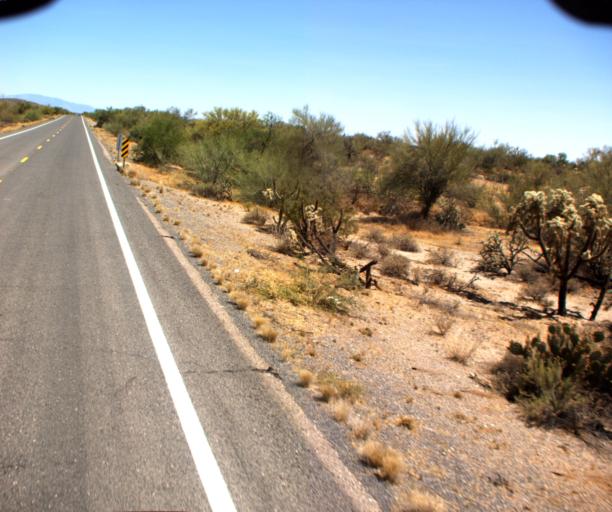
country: US
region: Arizona
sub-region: Pinal County
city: Florence
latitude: 32.8035
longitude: -111.1858
